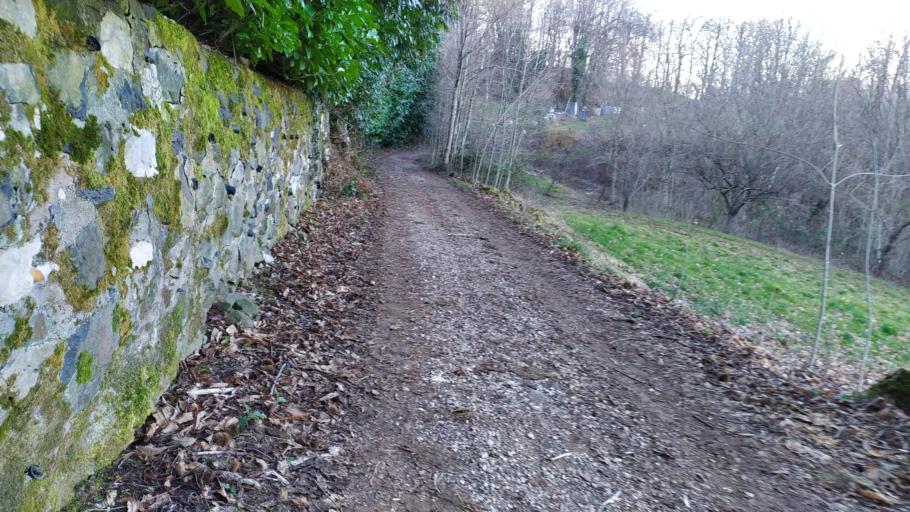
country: IT
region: Veneto
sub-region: Provincia di Vicenza
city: Monte di Malo
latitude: 45.6665
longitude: 11.3506
